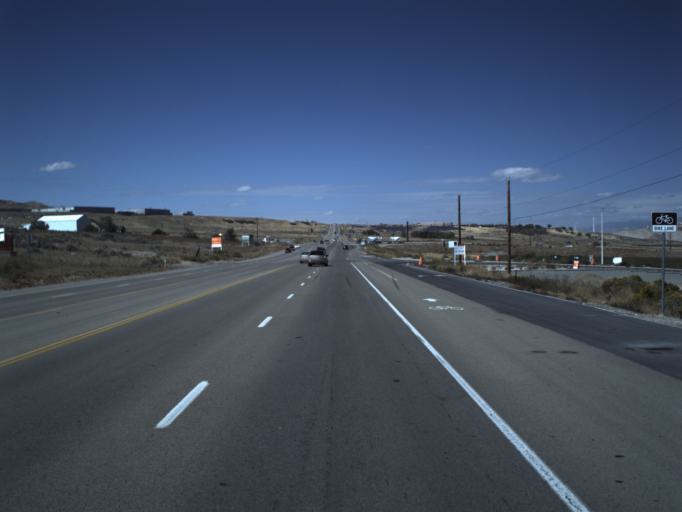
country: US
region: Utah
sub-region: Utah County
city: Saratoga Springs
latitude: 40.4088
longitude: -111.9218
